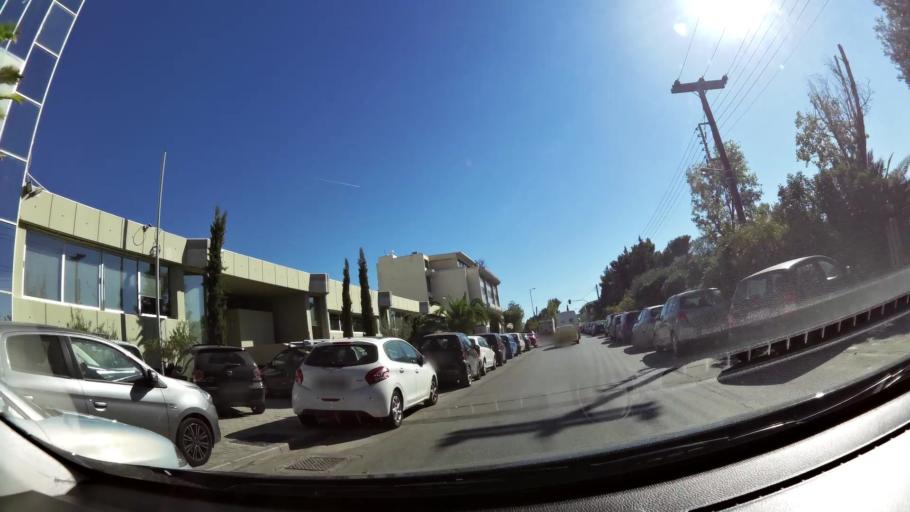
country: GR
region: Attica
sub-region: Nomarchia Athinas
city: Marousi
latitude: 38.0400
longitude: 23.8074
